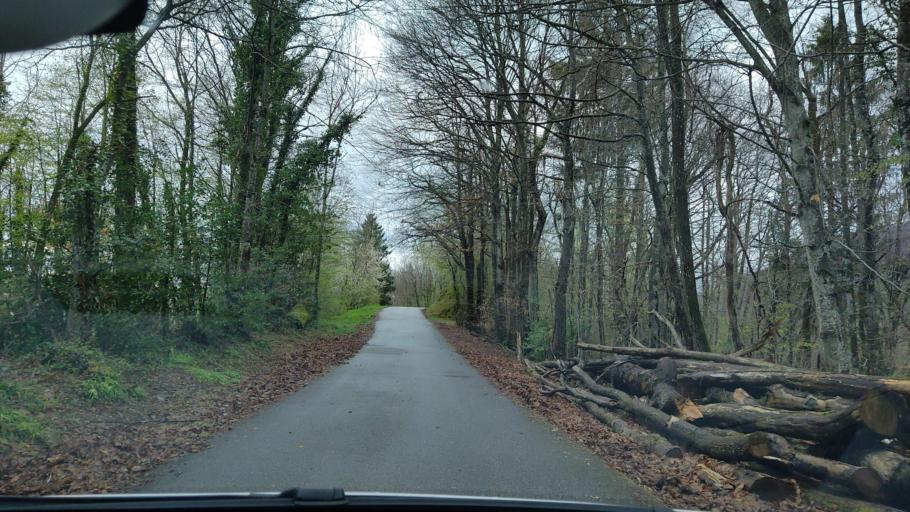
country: FR
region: Rhone-Alpes
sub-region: Departement de la Savoie
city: Vimines
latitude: 45.5501
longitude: 5.8154
